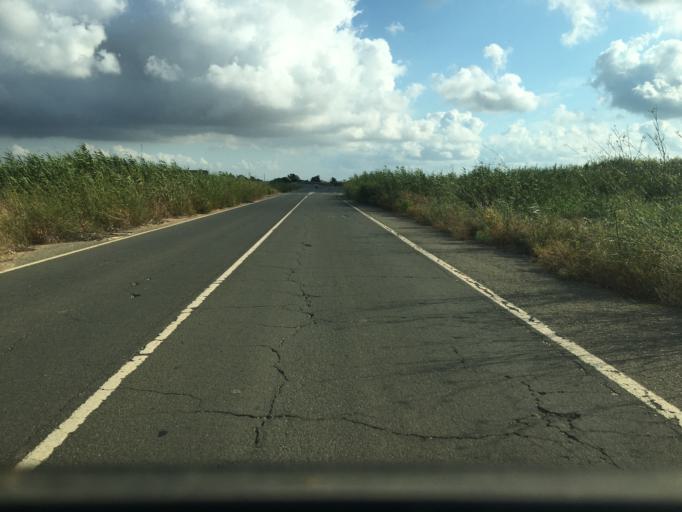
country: ES
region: Murcia
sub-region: Murcia
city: Los Alcazares
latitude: 37.7119
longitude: -0.8619
